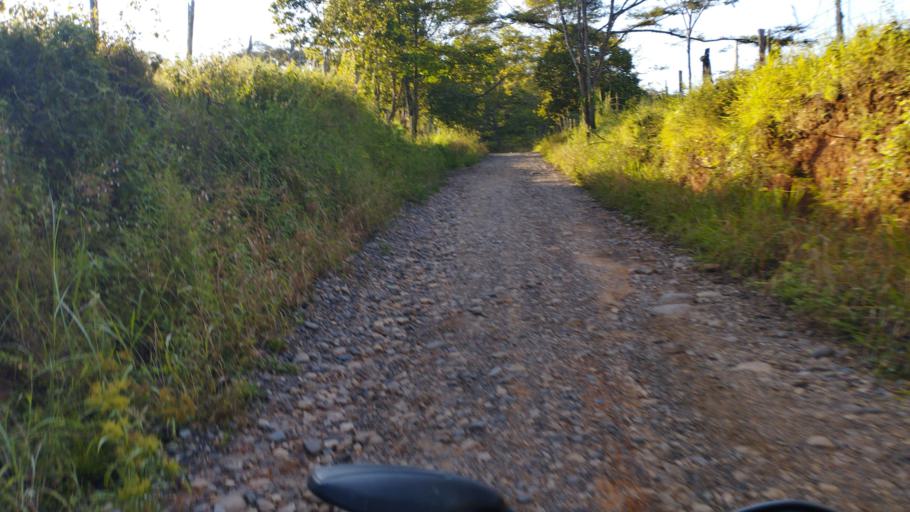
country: CO
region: Casanare
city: Sabanalarga
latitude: 4.8172
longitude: -73.0943
